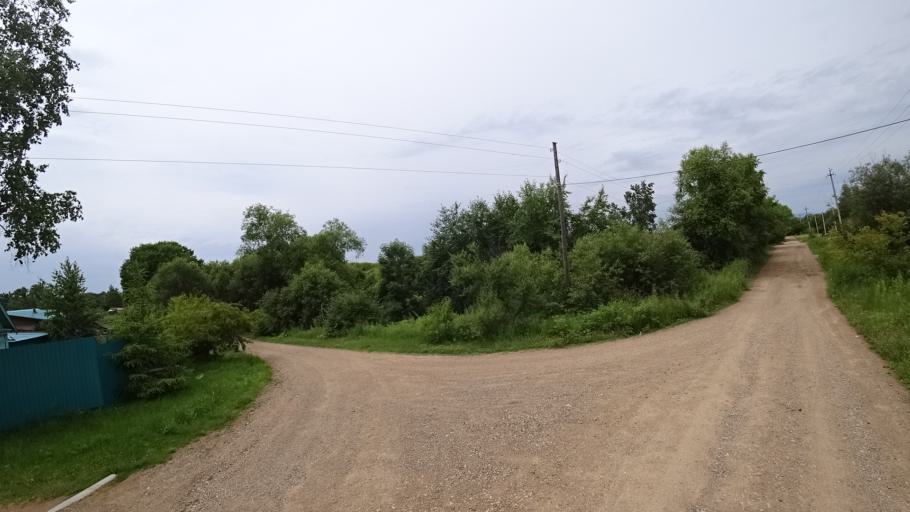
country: RU
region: Primorskiy
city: Arsen'yev
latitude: 44.1874
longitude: 133.3083
